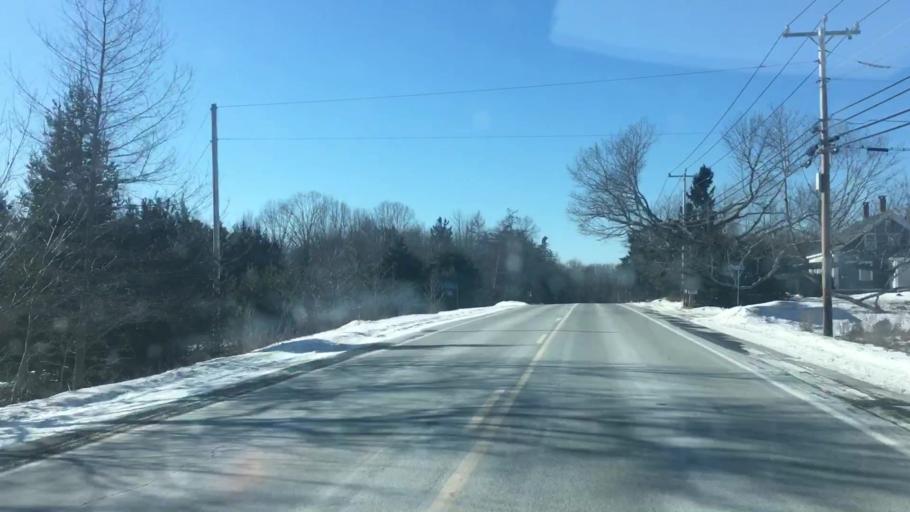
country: US
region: Maine
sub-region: Hancock County
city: Surry
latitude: 44.4934
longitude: -68.4550
